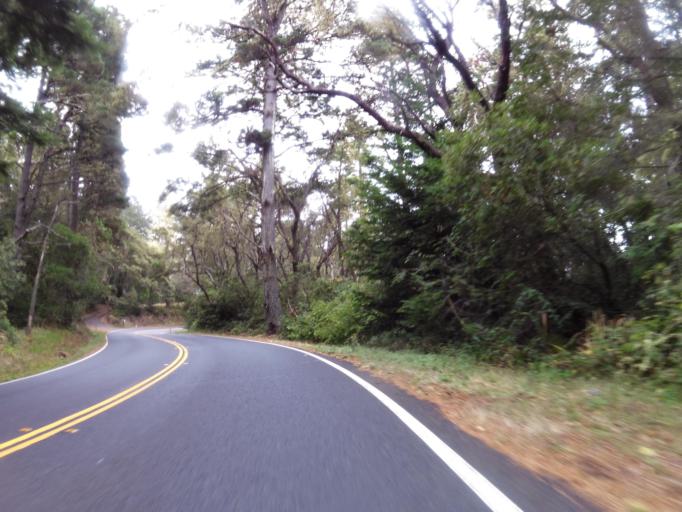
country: US
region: California
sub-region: Sonoma County
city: Sea Ranch
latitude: 38.5585
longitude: -123.3100
